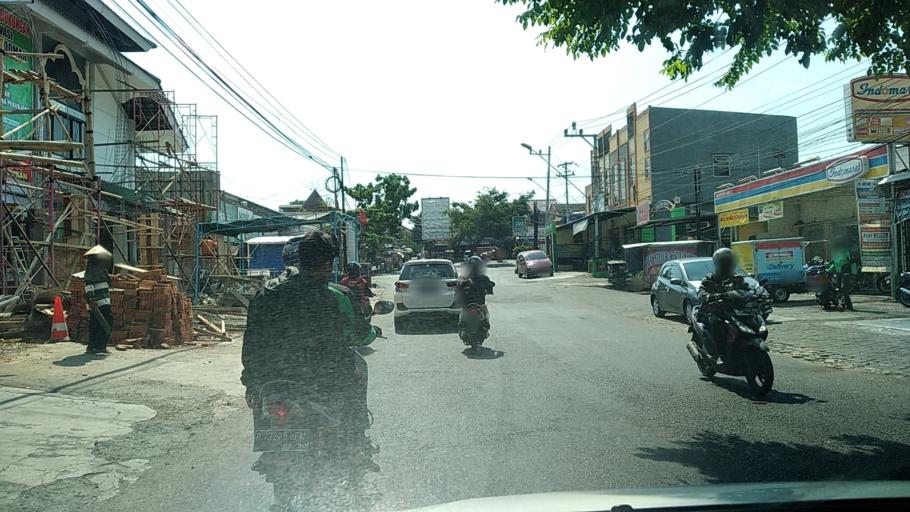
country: ID
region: Central Java
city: Ungaran
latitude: -7.0698
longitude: 110.4189
